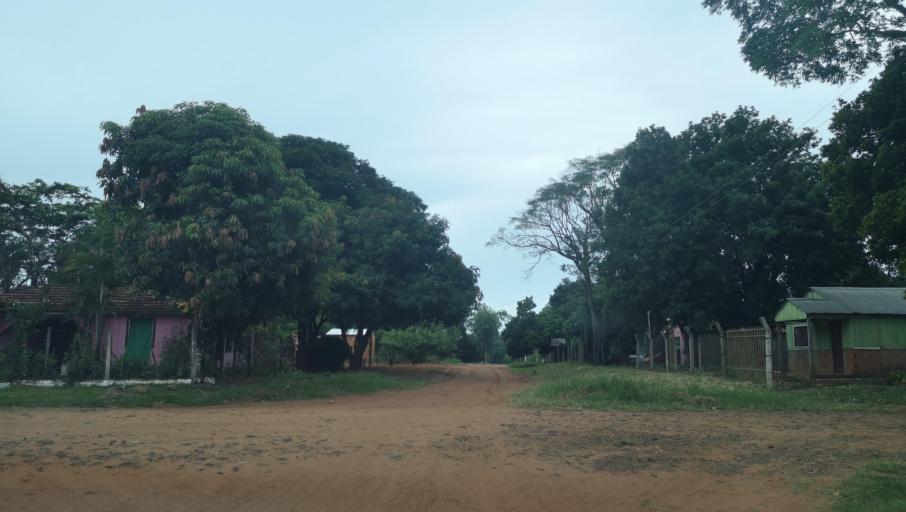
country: PY
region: San Pedro
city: Capiibary
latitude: -24.7266
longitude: -56.0120
